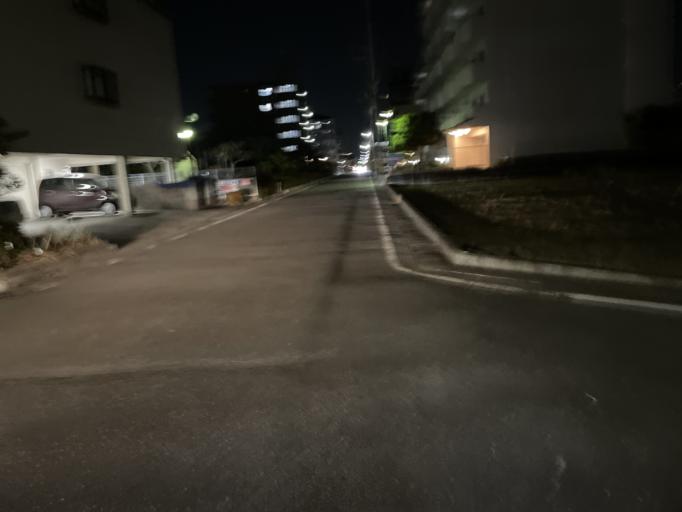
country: JP
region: Osaka
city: Ibaraki
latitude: 34.8007
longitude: 135.5831
